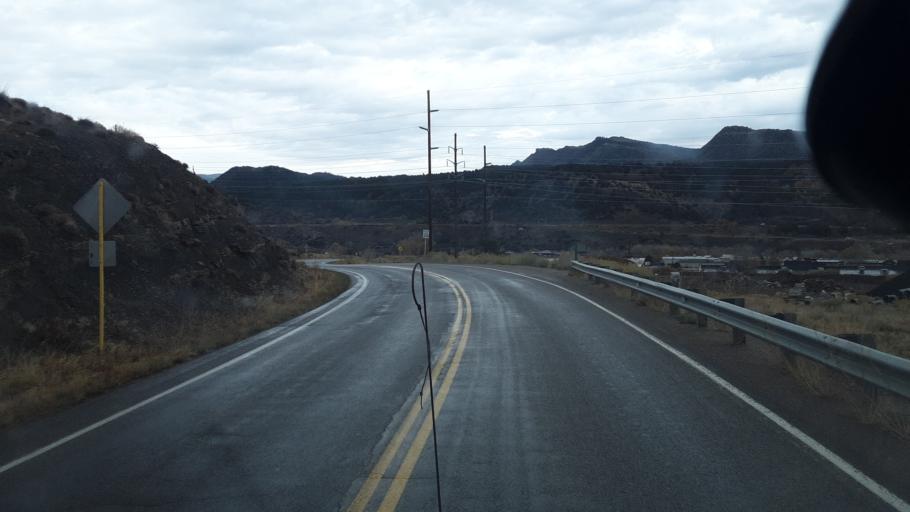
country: US
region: Colorado
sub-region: La Plata County
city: Durango
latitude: 37.2507
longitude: -107.8806
